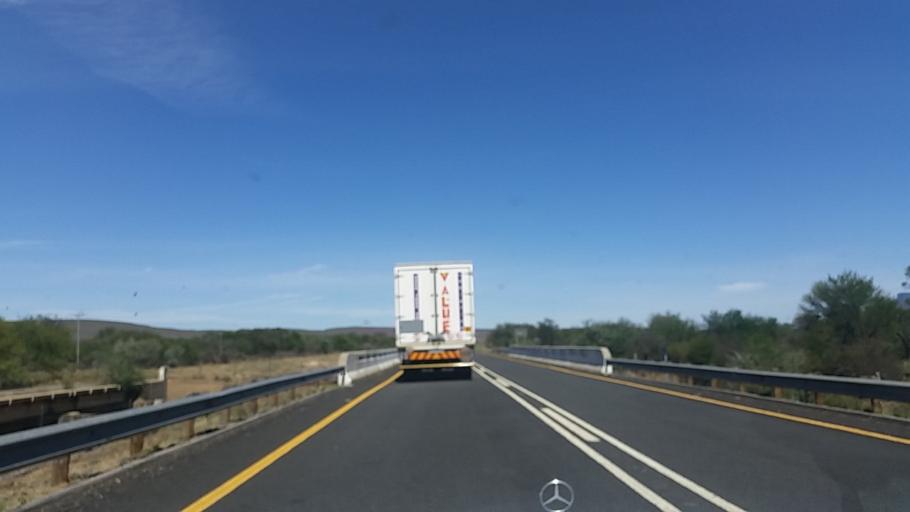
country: ZA
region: Eastern Cape
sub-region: Cacadu District Municipality
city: Graaff-Reinet
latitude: -32.3437
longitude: 24.3683
